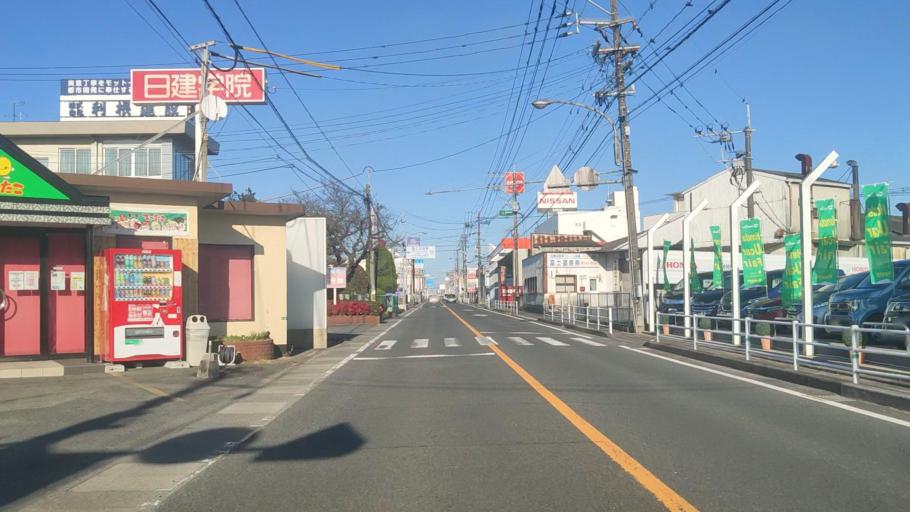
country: JP
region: Oita
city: Oita
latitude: 33.2138
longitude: 131.6102
